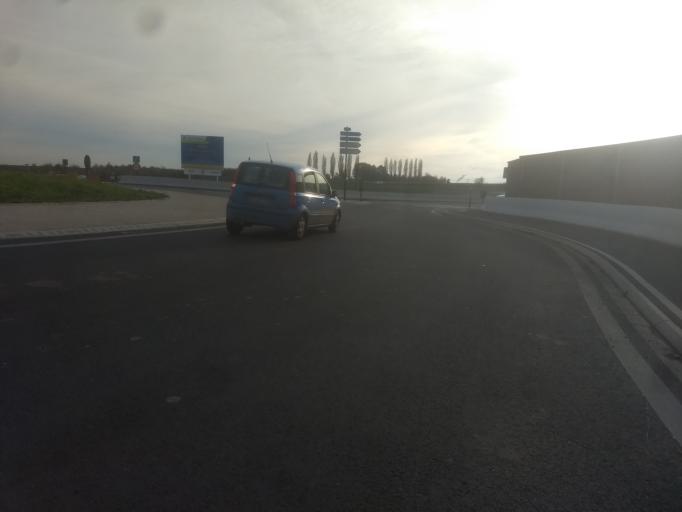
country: FR
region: Nord-Pas-de-Calais
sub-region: Departement du Pas-de-Calais
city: Agny
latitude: 50.2551
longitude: 2.7635
